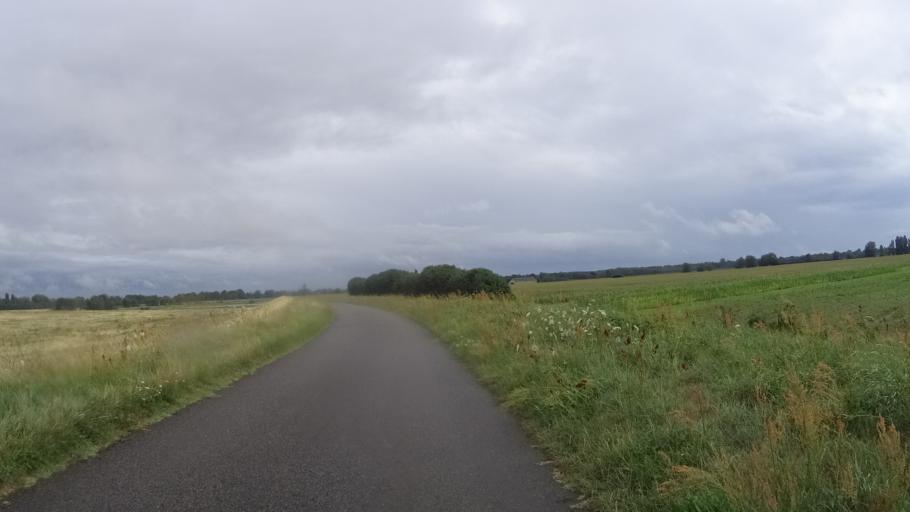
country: FR
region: Centre
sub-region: Departement du Loiret
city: Checy
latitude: 47.8831
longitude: 2.0104
